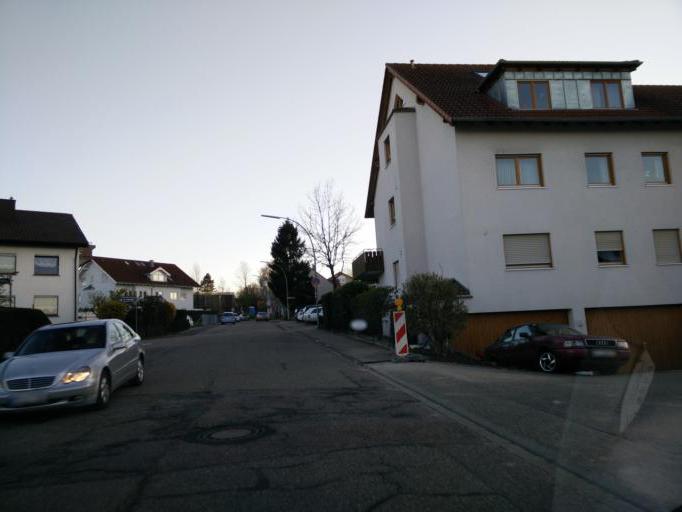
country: DE
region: Baden-Wuerttemberg
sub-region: Karlsruhe Region
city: Birkenfeld
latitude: 48.8579
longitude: 8.6564
